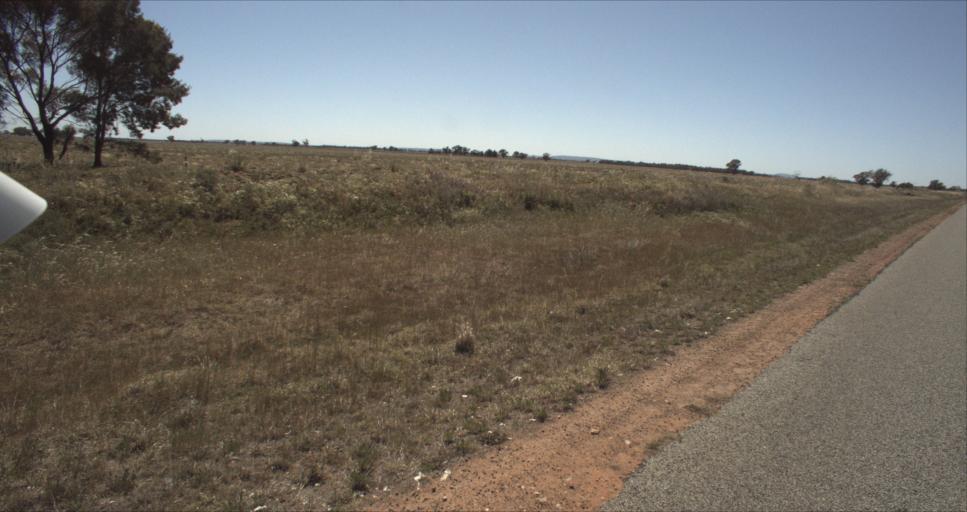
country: AU
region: New South Wales
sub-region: Leeton
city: Leeton
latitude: -34.5805
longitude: 146.2851
